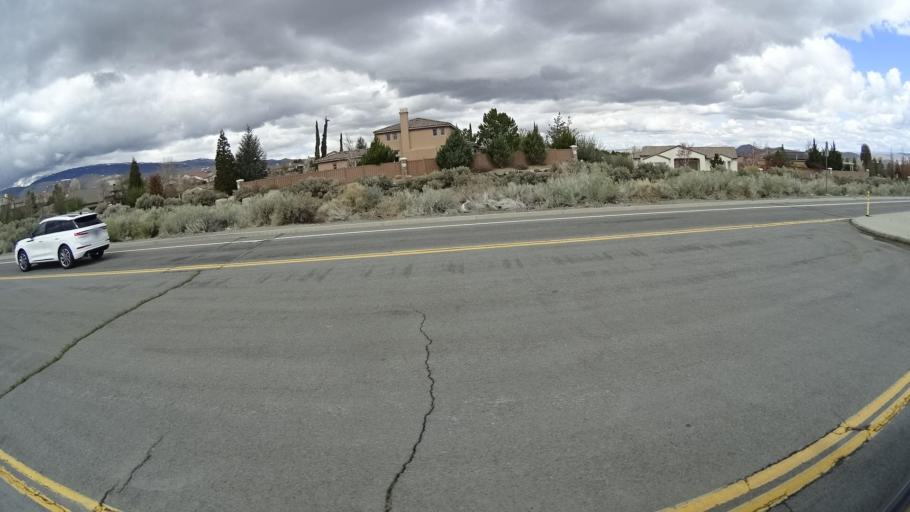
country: US
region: Nevada
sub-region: Washoe County
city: Sparks
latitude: 39.4076
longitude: -119.7623
